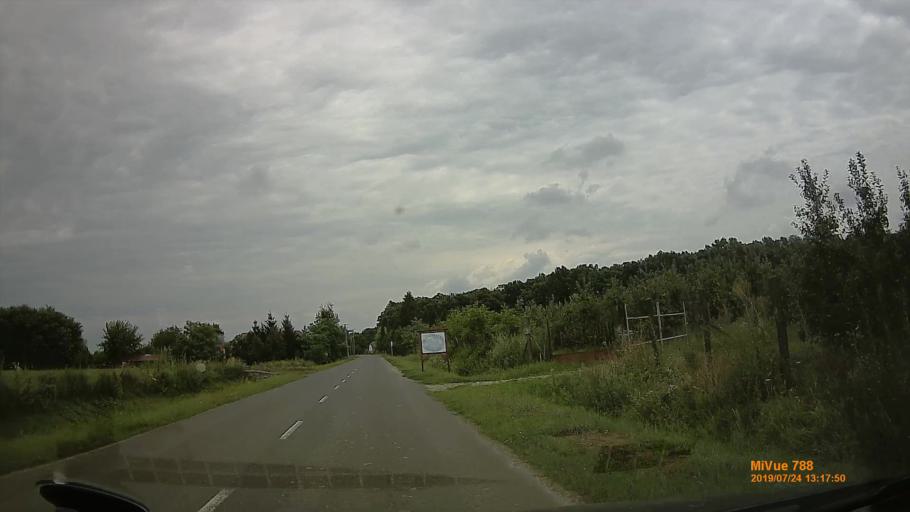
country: HU
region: Szabolcs-Szatmar-Bereg
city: Vasarosnameny
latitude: 48.1922
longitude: 22.3946
